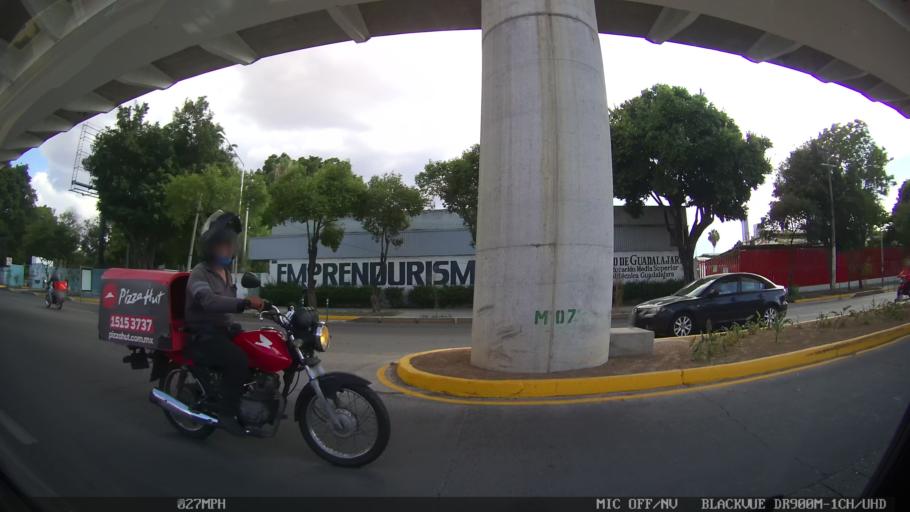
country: MX
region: Jalisco
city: Tlaquepaque
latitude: 20.6599
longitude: -103.3243
